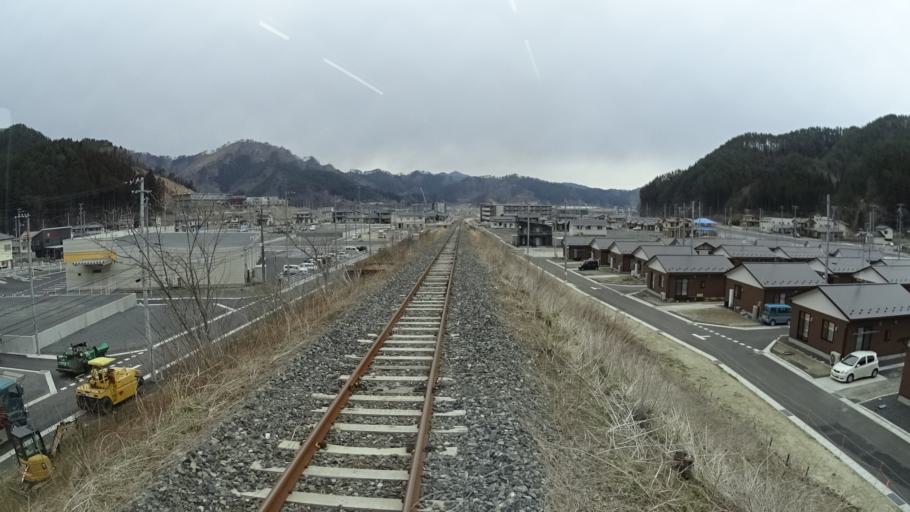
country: JP
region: Iwate
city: Kamaishi
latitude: 39.3210
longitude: 141.8851
